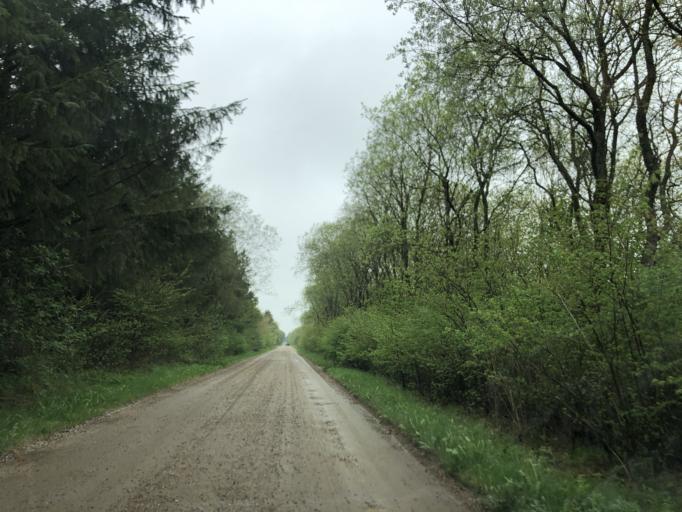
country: DK
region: Central Jutland
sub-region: Lemvig Kommune
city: Lemvig
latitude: 56.5076
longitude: 8.3215
